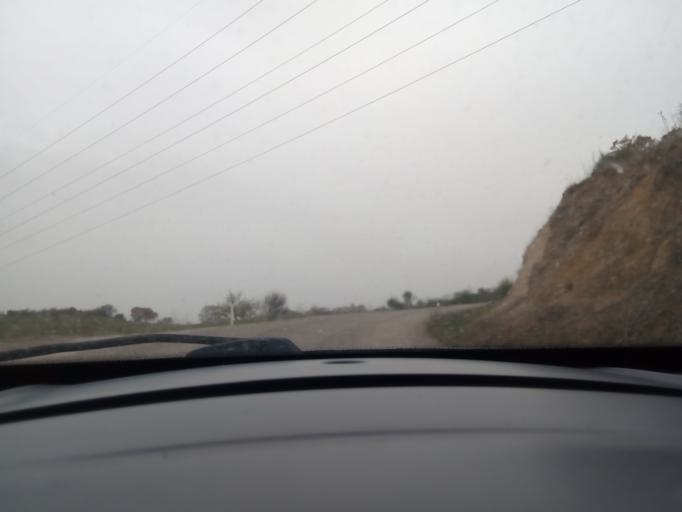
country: TR
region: Balikesir
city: Susurluk
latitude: 39.9085
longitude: 28.1095
